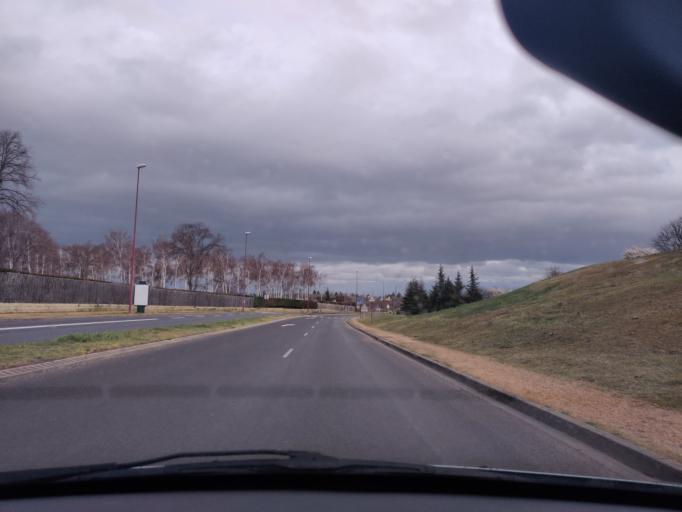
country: FR
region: Auvergne
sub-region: Departement du Puy-de-Dome
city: Chatel-Guyon
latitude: 45.9145
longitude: 3.0773
